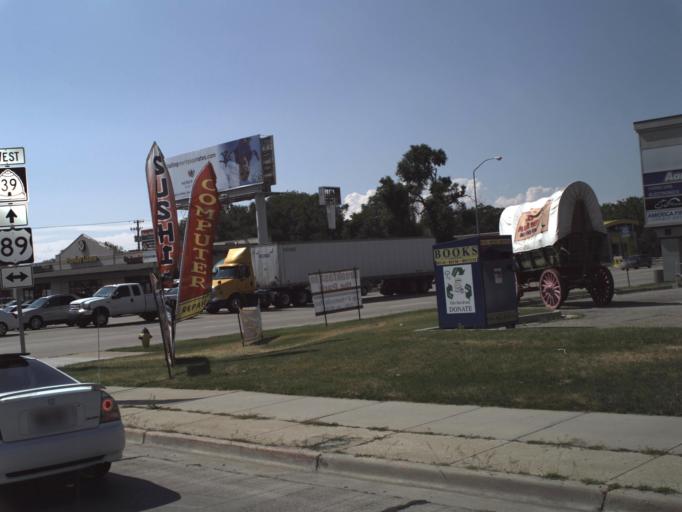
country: US
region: Utah
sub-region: Weber County
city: Ogden
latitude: 41.2443
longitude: -111.9662
